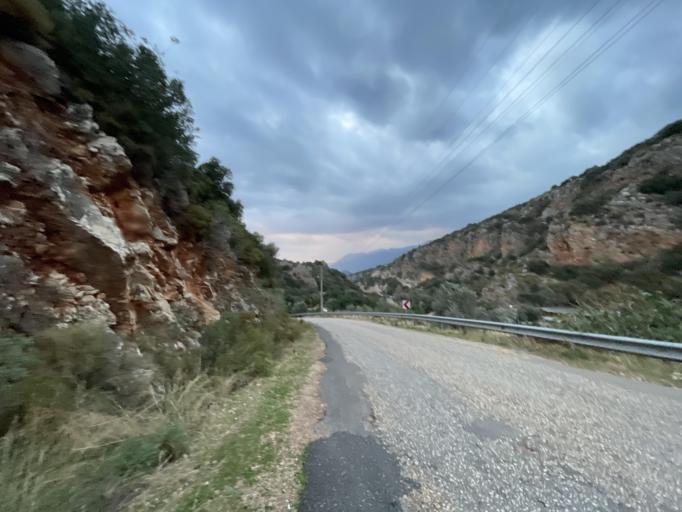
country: TR
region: Antalya
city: Kas
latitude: 36.1905
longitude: 29.6549
